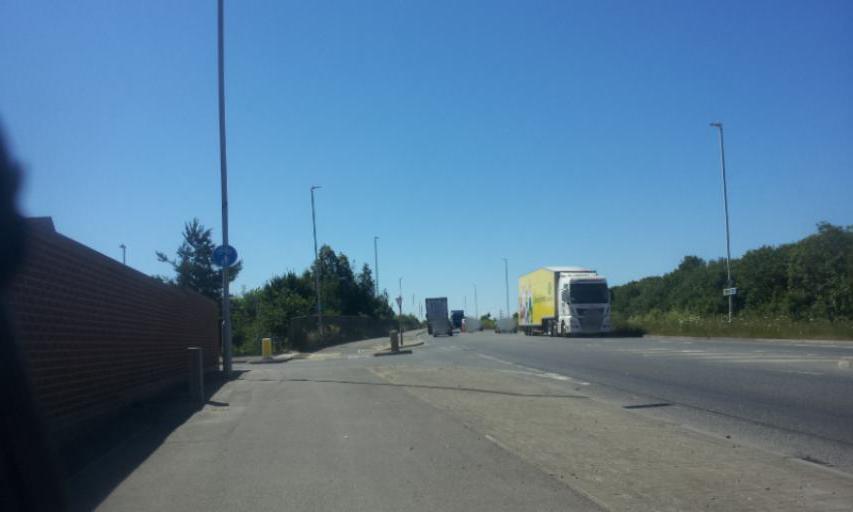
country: GB
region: England
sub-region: Kent
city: Sittingbourne
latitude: 51.3656
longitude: 0.7436
